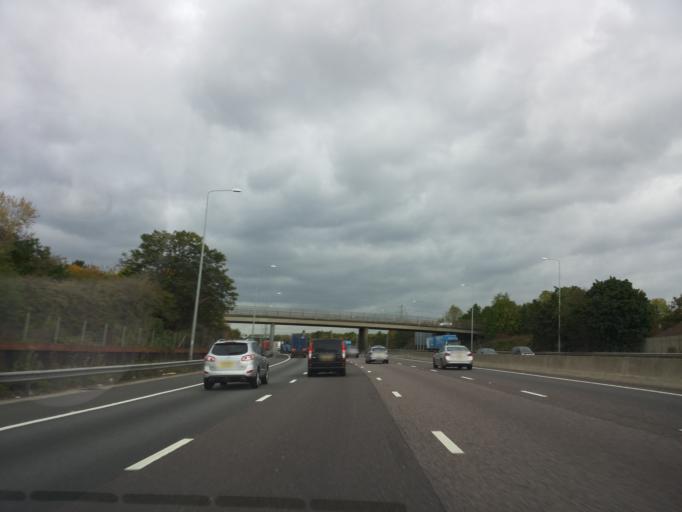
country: GB
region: England
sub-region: Hertfordshire
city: Shenley AV
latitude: 51.7100
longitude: -0.2975
